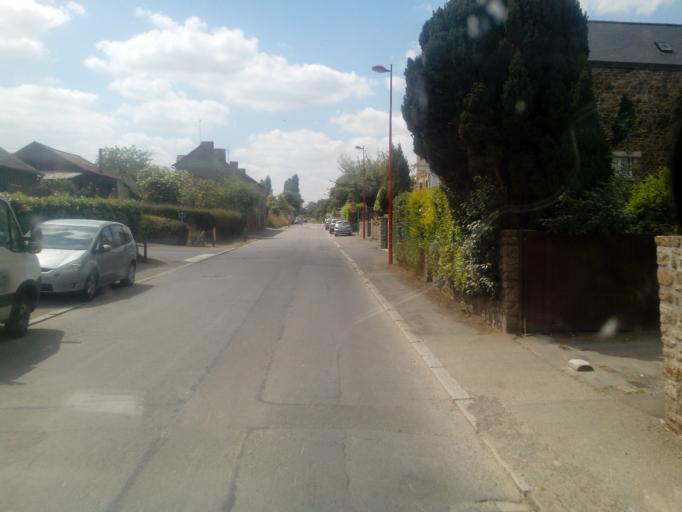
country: FR
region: Brittany
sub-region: Departement d'Ille-et-Vilaine
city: Sens-de-Bretagne
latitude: 48.3330
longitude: -1.5390
